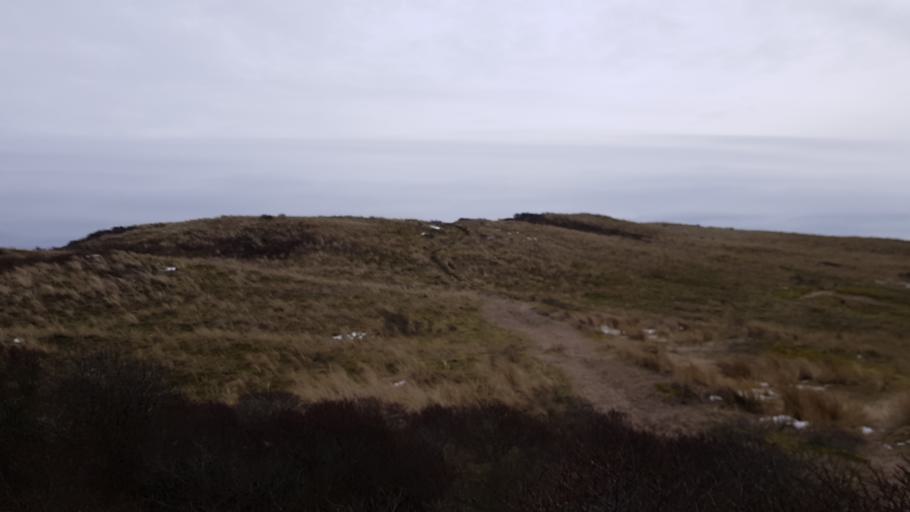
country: NL
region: North Holland
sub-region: Gemeente Bergen
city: Egmond aan Zee
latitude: 52.5755
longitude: 4.6173
